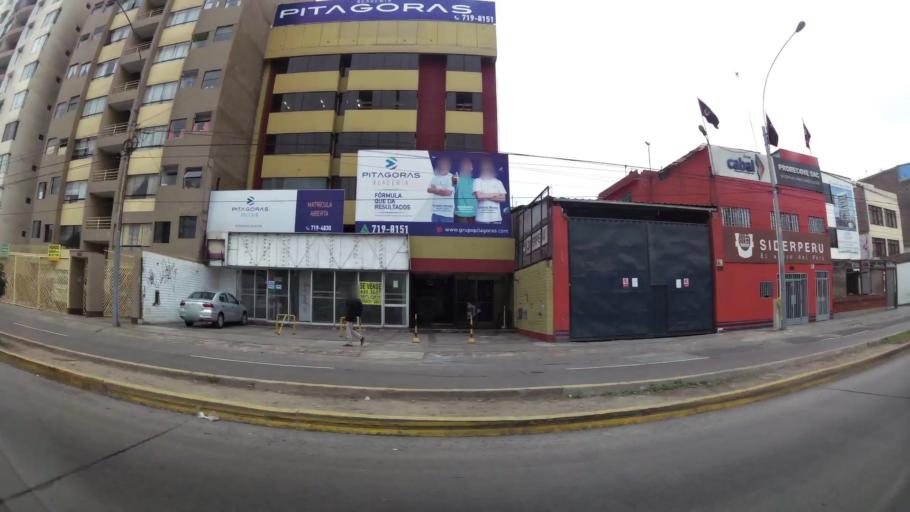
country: PE
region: Callao
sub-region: Callao
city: Callao
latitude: -12.0709
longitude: -77.0985
